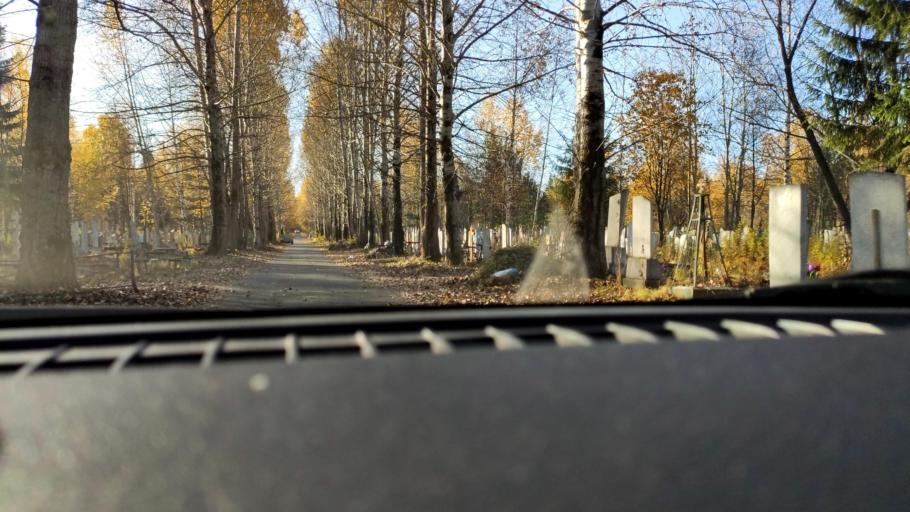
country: RU
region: Perm
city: Kondratovo
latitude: 58.0652
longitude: 56.1365
